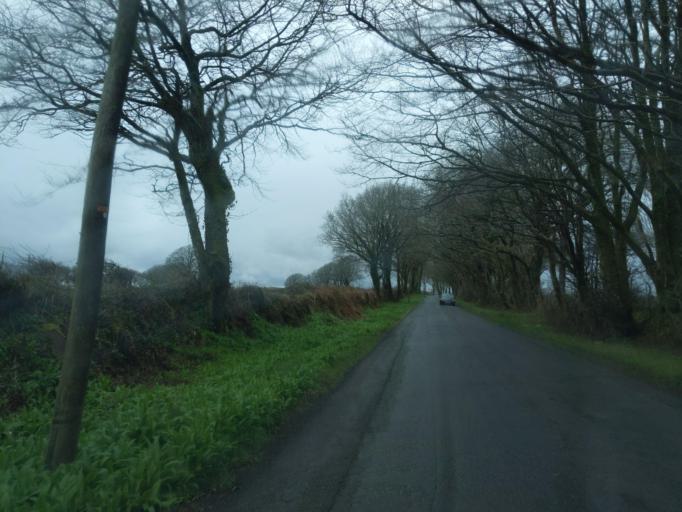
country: GB
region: England
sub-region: Cornwall
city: Trewen
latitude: 50.5924
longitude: -4.4377
